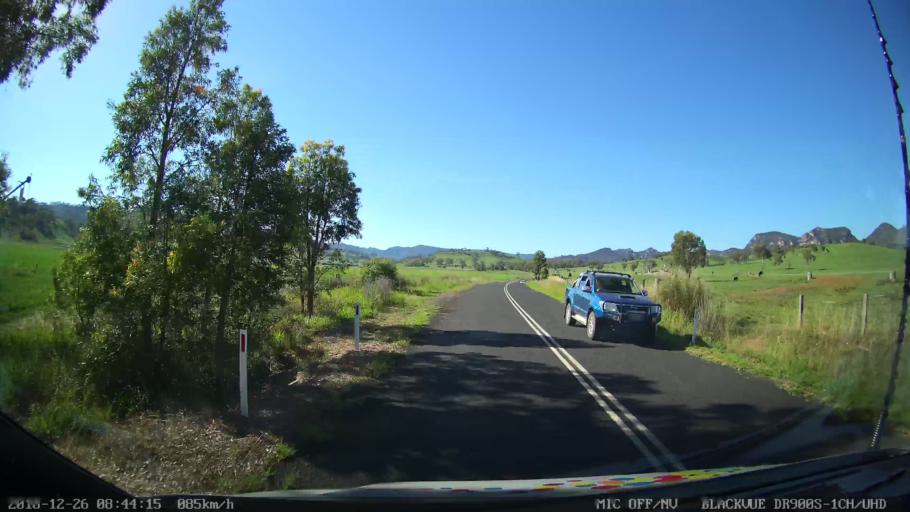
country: AU
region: New South Wales
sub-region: Mid-Western Regional
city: Kandos
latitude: -32.5123
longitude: 150.0808
